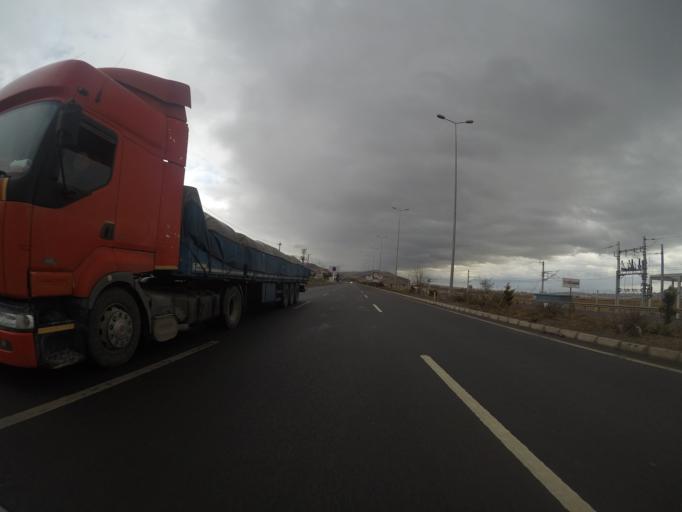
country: TR
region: Kayseri
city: Melikgazi
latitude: 38.7467
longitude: 35.3039
